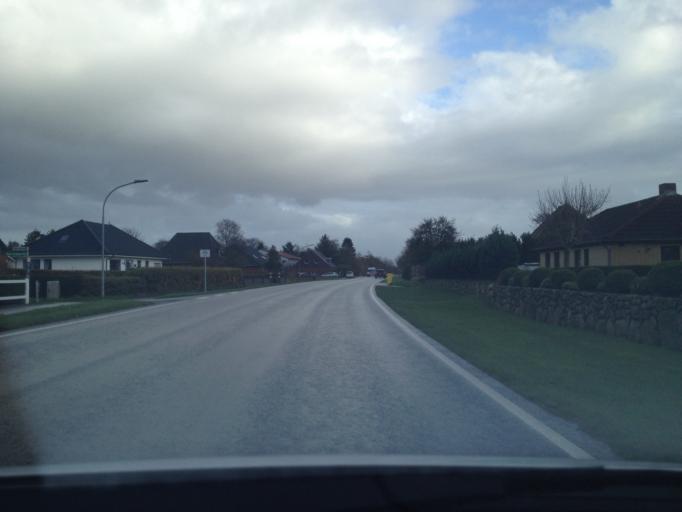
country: DE
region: Schleswig-Holstein
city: Klixbull
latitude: 54.7936
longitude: 8.9095
